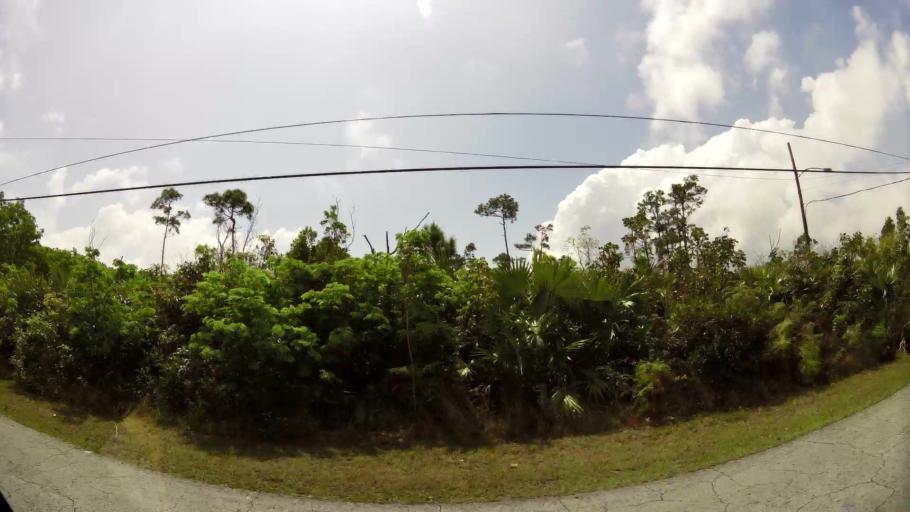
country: BS
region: Freeport
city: Lucaya
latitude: 26.5338
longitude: -78.6274
